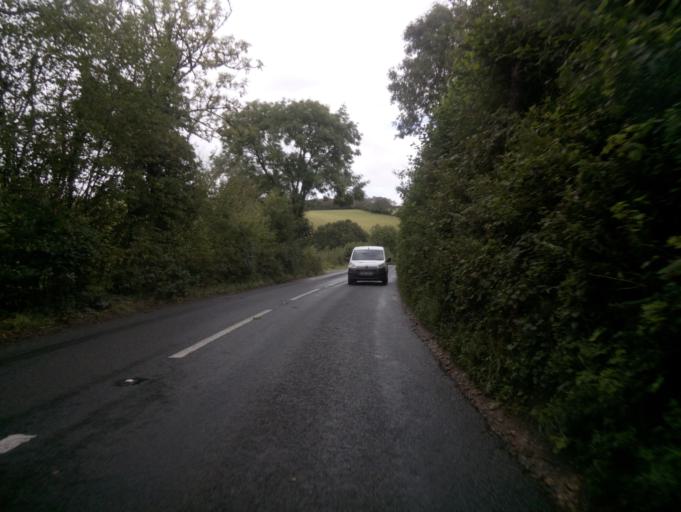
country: GB
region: England
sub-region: Devon
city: Modbury
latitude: 50.3301
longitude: -3.8447
